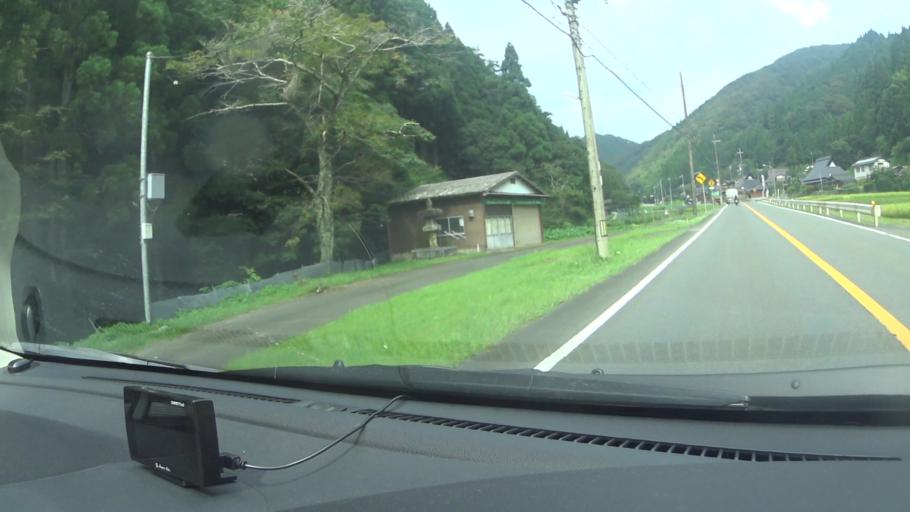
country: JP
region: Kyoto
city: Ayabe
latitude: 35.2312
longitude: 135.3337
